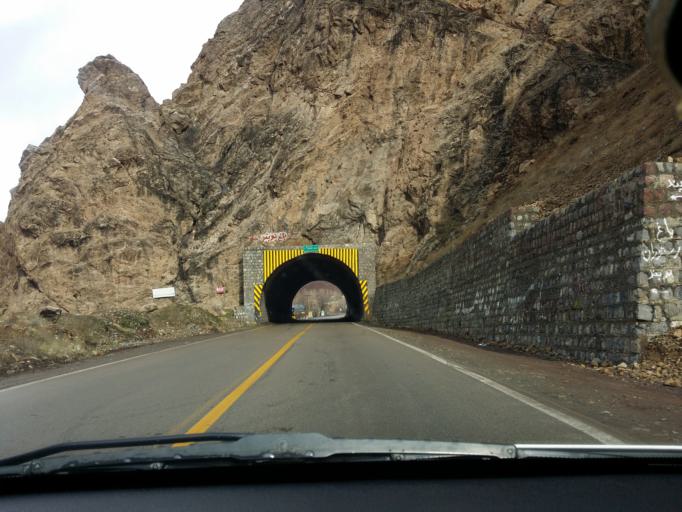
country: IR
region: Tehran
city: Tajrish
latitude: 36.0477
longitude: 51.3135
